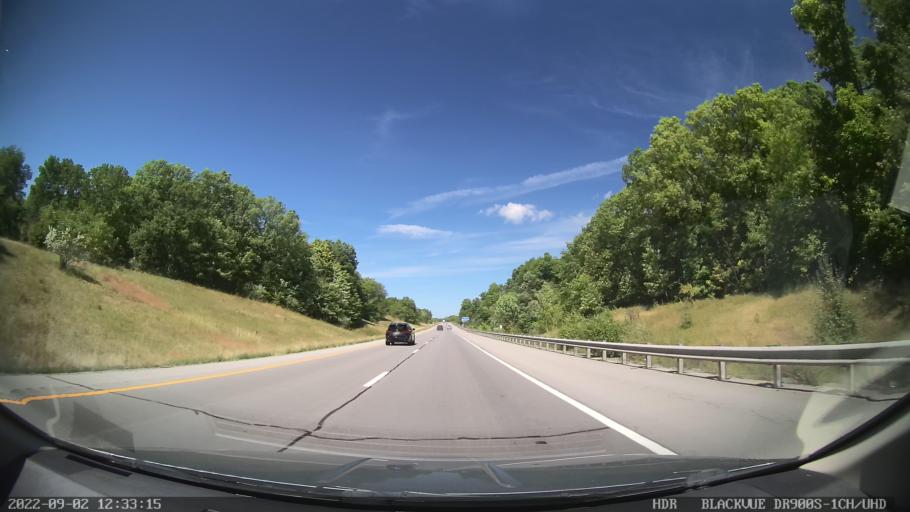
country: US
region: New York
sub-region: Livingston County
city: Dansville
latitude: 42.6348
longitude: -77.7835
